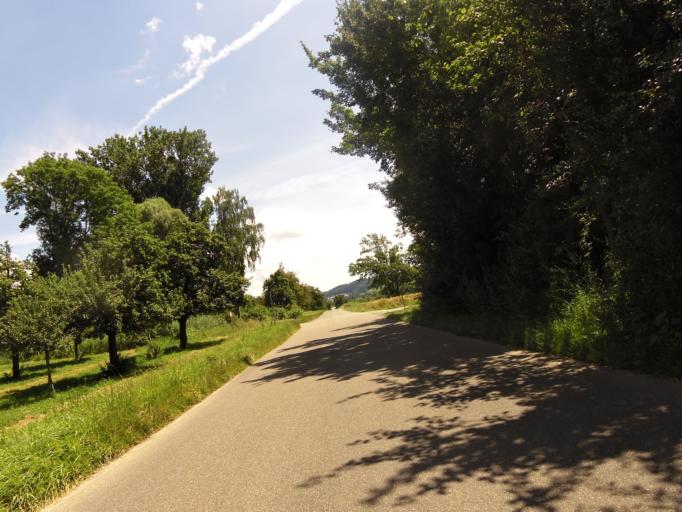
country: DE
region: Baden-Wuerttemberg
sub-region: Tuebingen Region
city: Uhldingen-Muhlhofen
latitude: 47.7405
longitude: 9.2284
